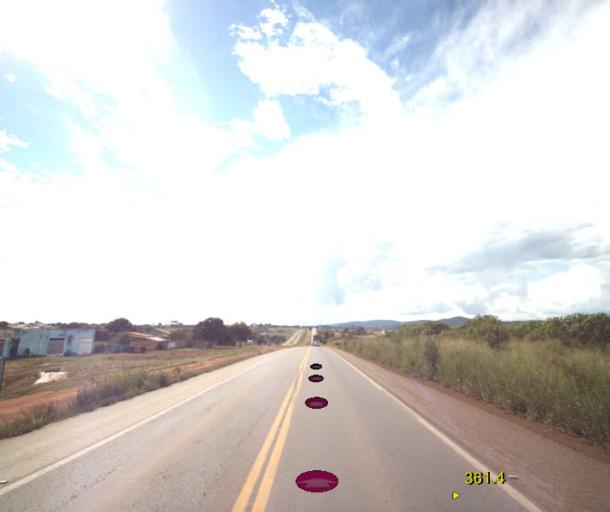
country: BR
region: Goias
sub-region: Jaragua
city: Jaragua
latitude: -15.7520
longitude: -49.3162
